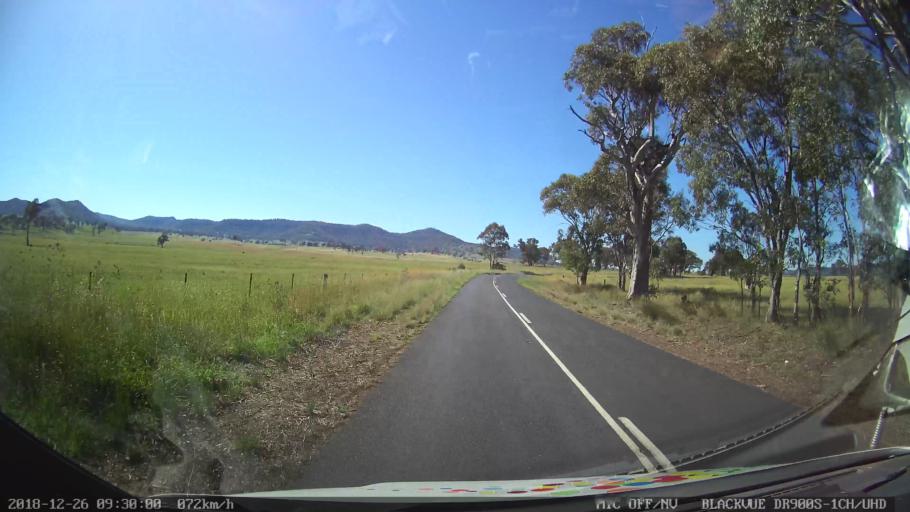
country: AU
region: New South Wales
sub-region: Mid-Western Regional
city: Kandos
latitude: -32.8587
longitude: 150.0302
